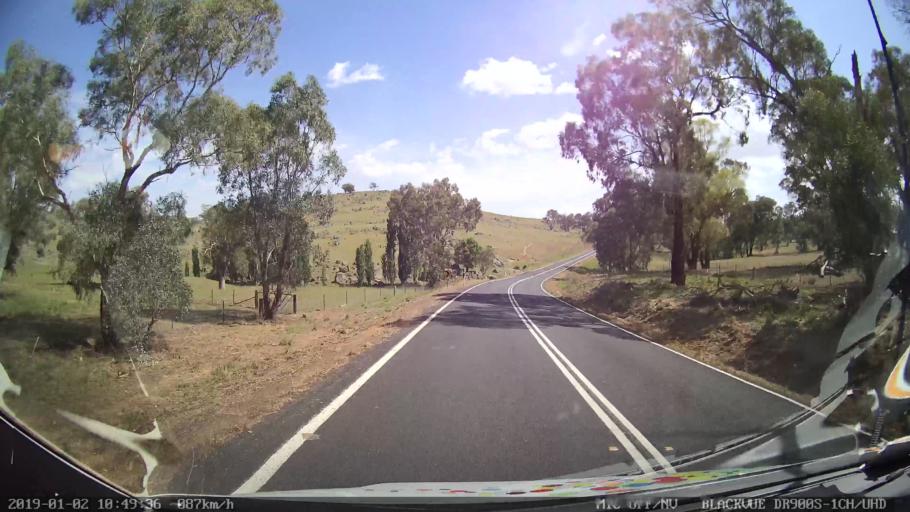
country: AU
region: New South Wales
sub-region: Cootamundra
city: Cootamundra
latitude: -34.7222
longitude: 148.2759
